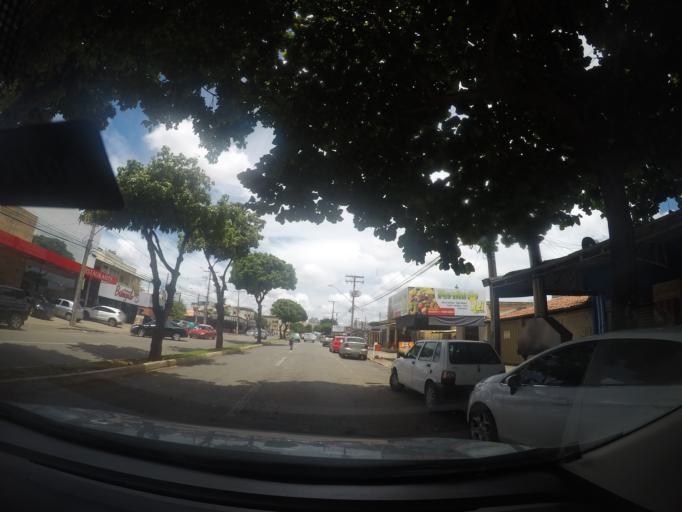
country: BR
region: Goias
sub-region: Goiania
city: Goiania
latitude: -16.6905
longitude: -49.3014
